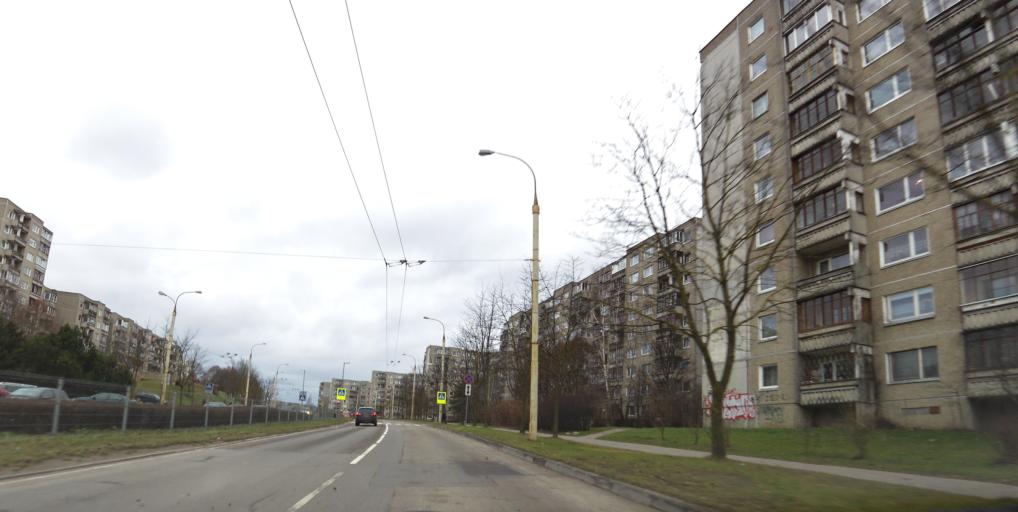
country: LT
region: Vilnius County
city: Justiniskes
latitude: 54.7190
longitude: 25.2228
